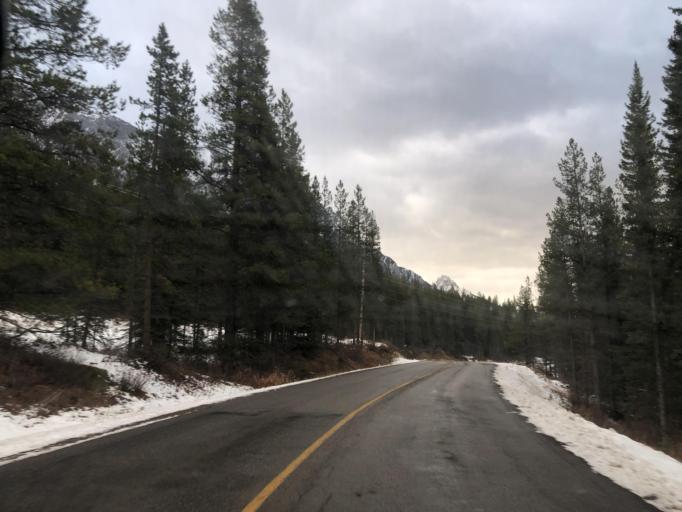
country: CA
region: Alberta
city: Canmore
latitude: 50.7105
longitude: -115.1141
